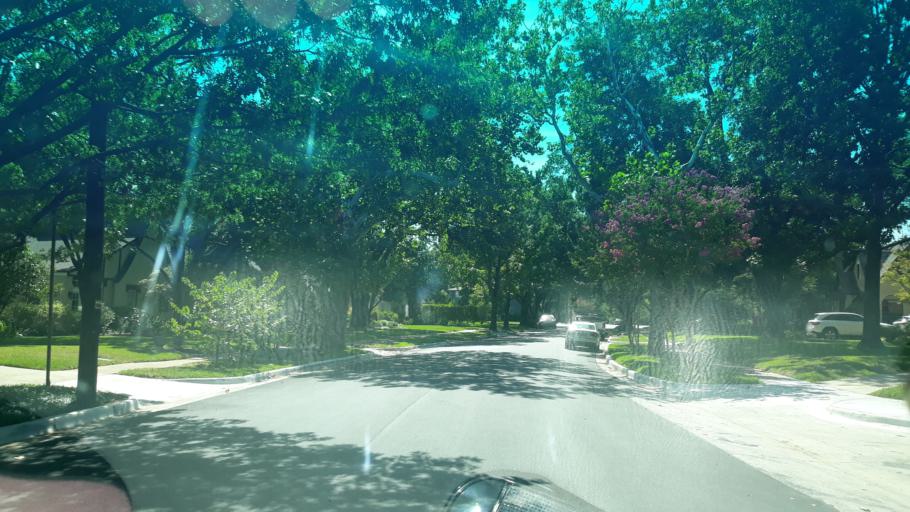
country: US
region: Texas
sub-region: Dallas County
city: Highland Park
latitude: 32.8192
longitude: -96.7515
